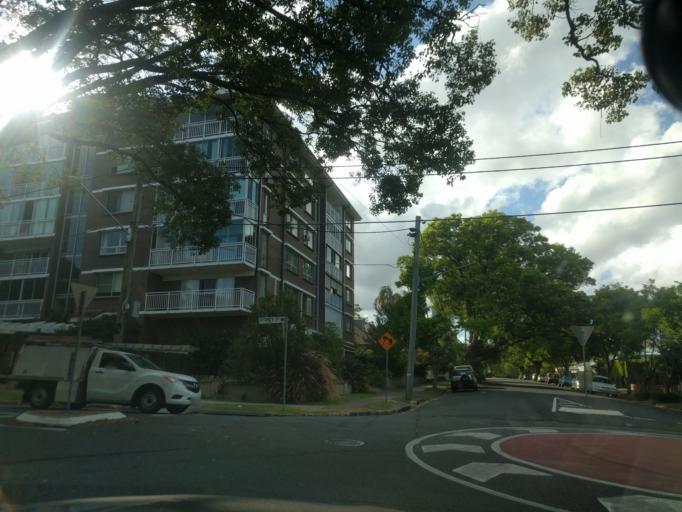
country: AU
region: Queensland
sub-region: Brisbane
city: Brisbane
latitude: -27.4709
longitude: 153.0458
